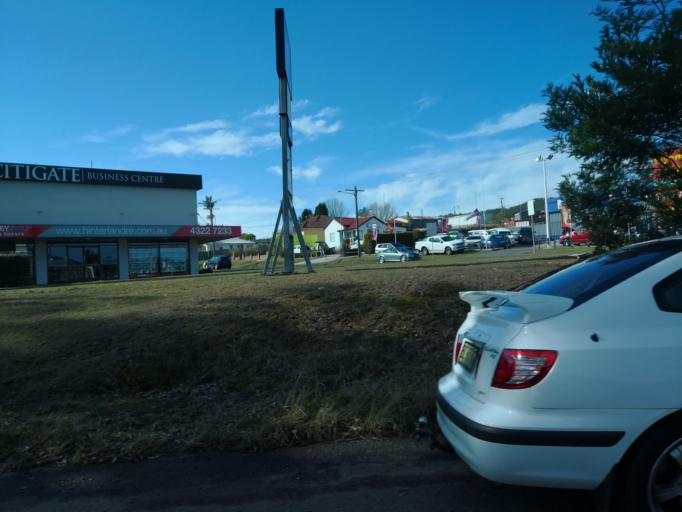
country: AU
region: New South Wales
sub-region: Gosford Shire
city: Narara
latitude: -33.4110
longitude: 151.3467
